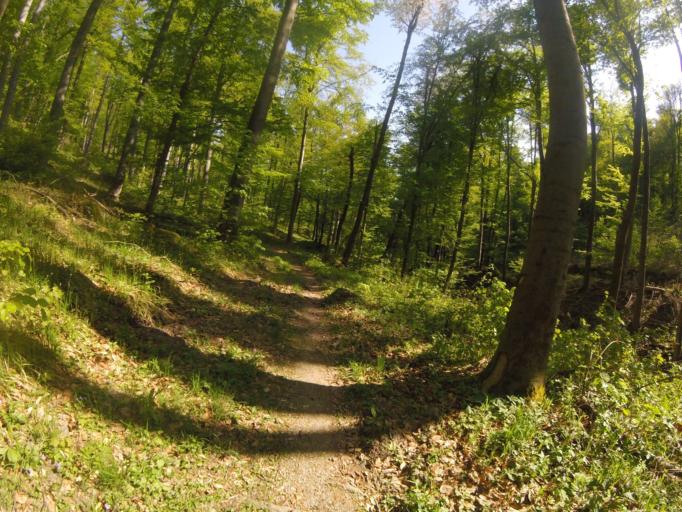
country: HU
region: Pest
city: Pilisszentkereszt
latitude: 47.7128
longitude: 18.8917
